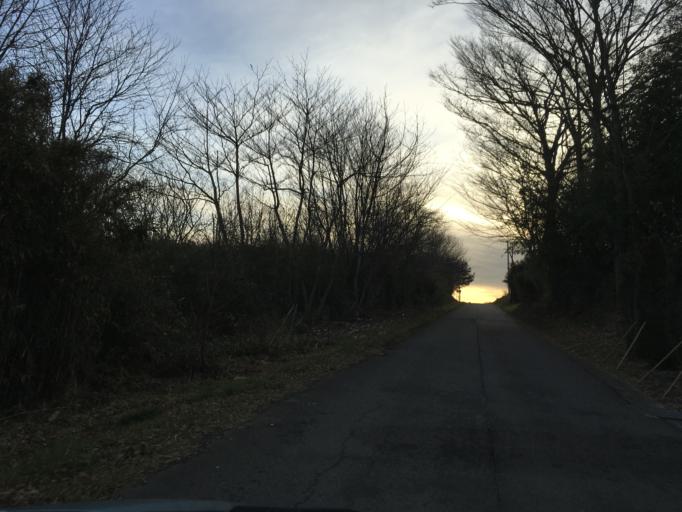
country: JP
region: Miyagi
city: Kogota
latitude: 38.6736
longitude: 141.0877
